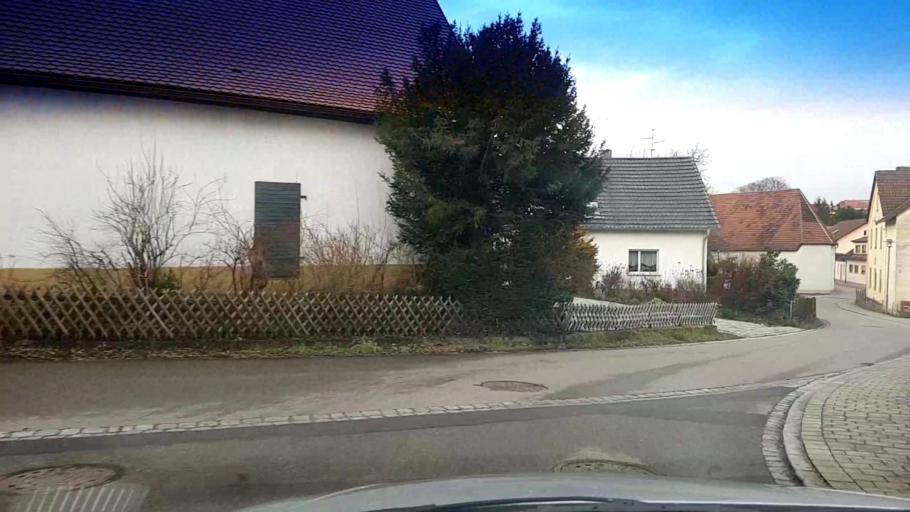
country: DE
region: Bavaria
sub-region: Upper Franconia
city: Litzendorf
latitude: 49.9085
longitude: 11.0031
